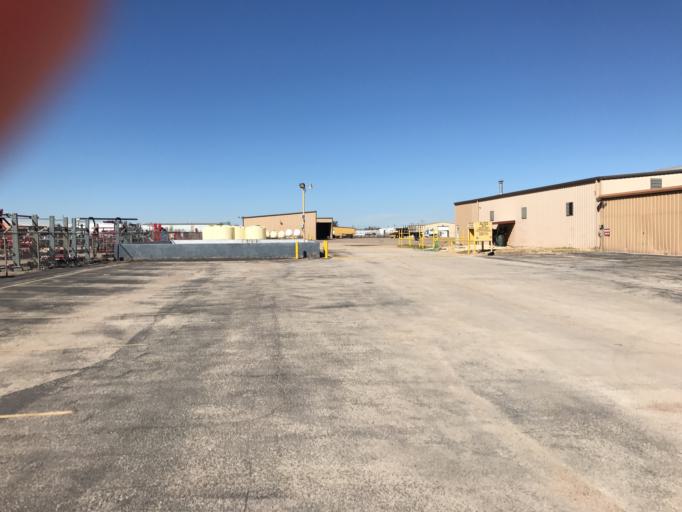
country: US
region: Texas
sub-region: Ector County
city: Odessa
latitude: 31.8983
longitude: -102.2426
